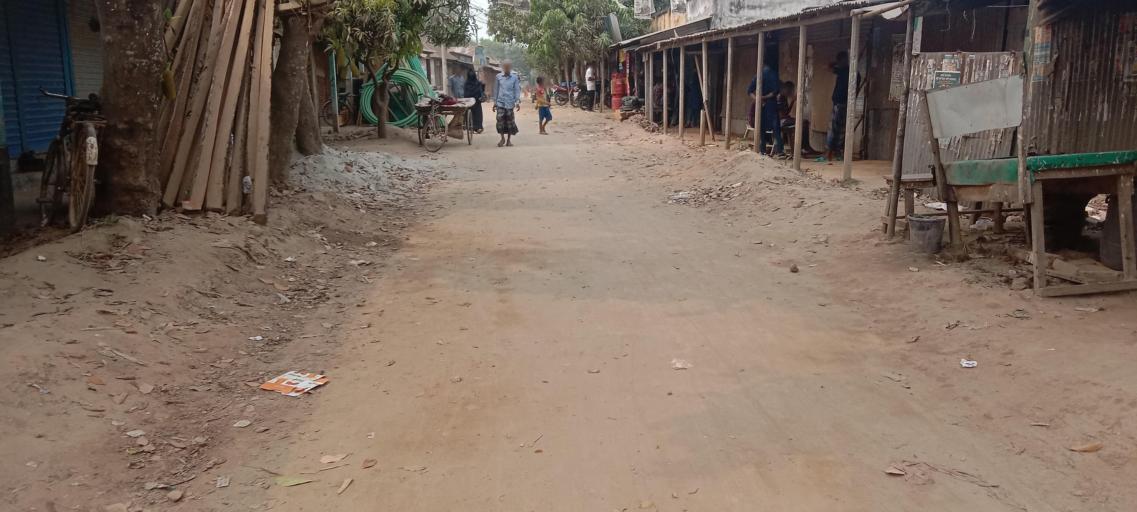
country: BD
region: Dhaka
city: Gafargaon
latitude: 24.4559
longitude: 90.4643
